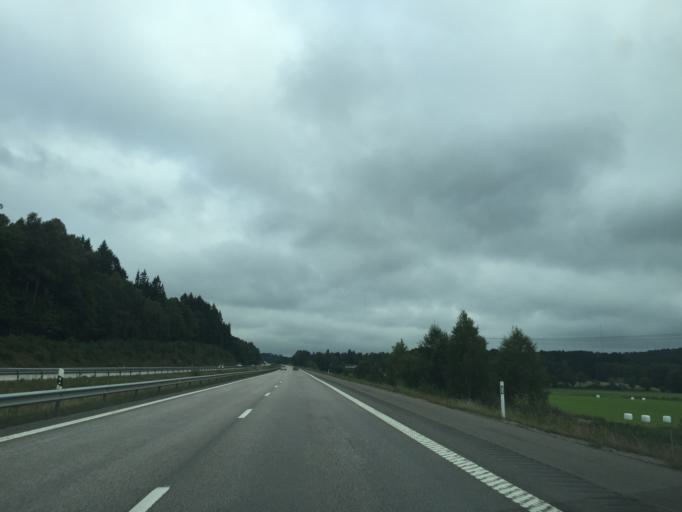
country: SE
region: Halland
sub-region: Kungsbacka Kommun
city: Frillesas
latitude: 57.3685
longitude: 12.2040
